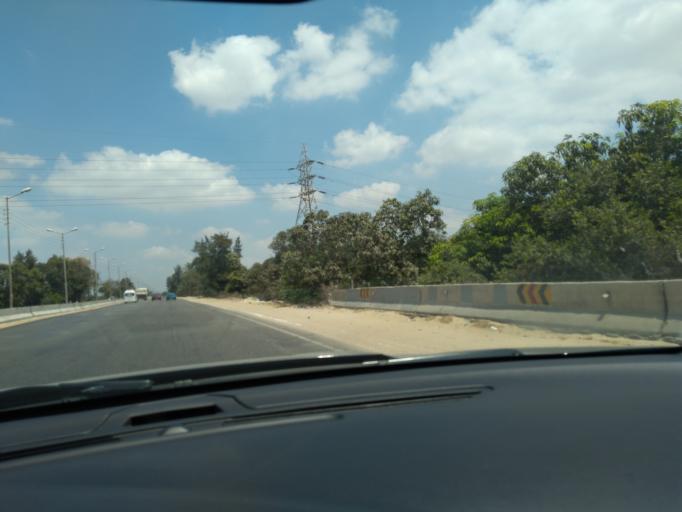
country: EG
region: Al Isma'iliyah
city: Ismailia
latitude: 30.6437
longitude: 32.2595
